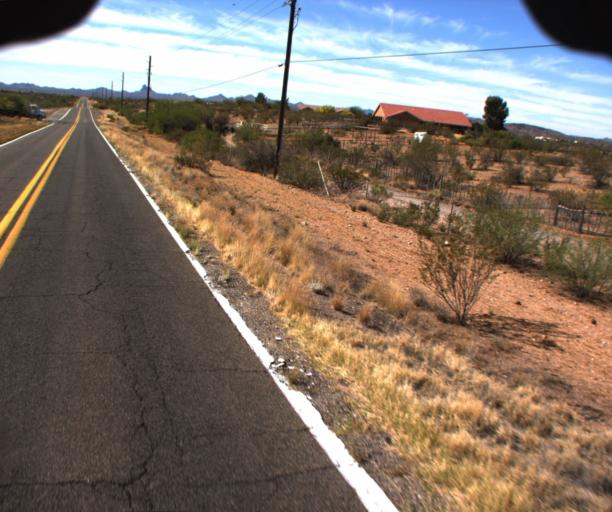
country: US
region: Arizona
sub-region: Maricopa County
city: Wickenburg
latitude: 34.0471
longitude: -112.8152
